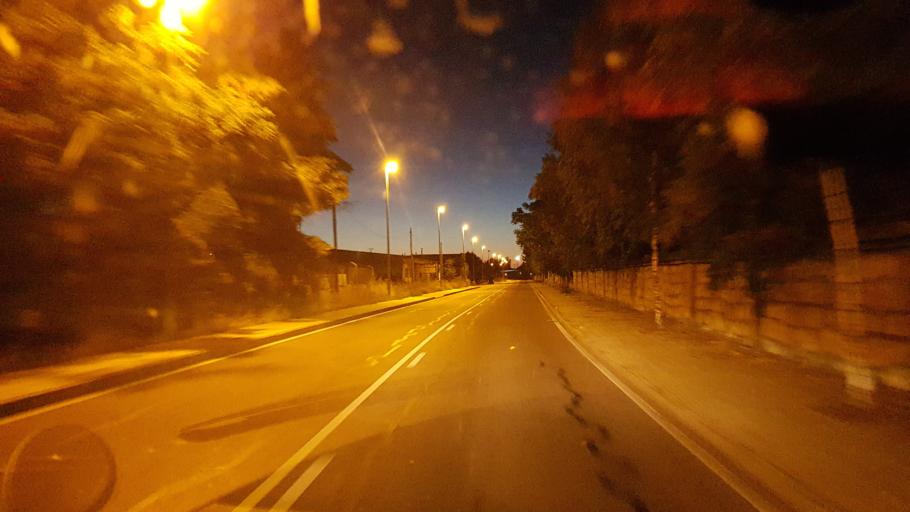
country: ES
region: Castille and Leon
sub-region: Provincia de Zamora
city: Zamora
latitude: 41.5189
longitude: -5.7377
